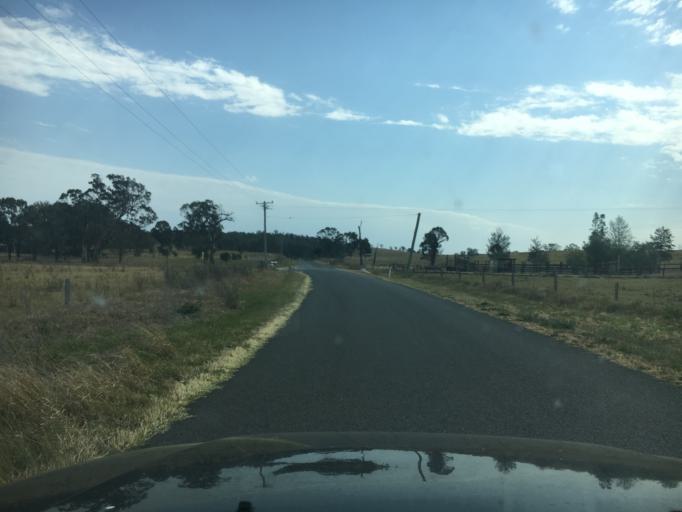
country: AU
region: New South Wales
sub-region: Cessnock
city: Branxton
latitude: -32.5076
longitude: 151.3167
